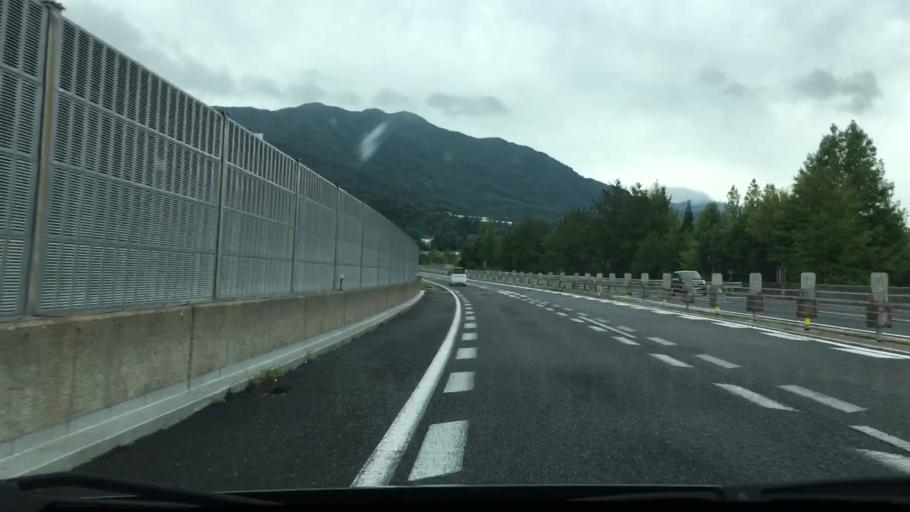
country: JP
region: Hiroshima
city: Hiroshima-shi
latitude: 34.6487
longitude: 132.5167
